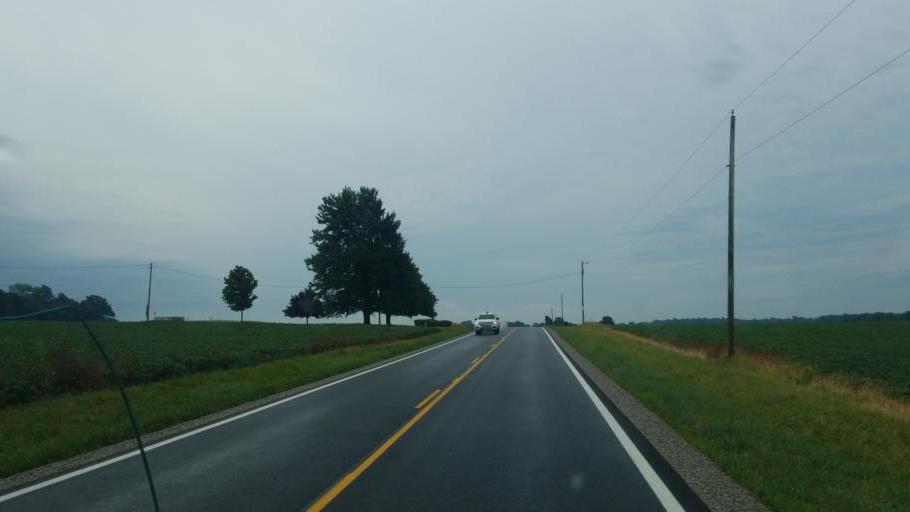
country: US
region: Ohio
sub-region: Williams County
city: Edgerton
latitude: 41.3778
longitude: -84.6697
